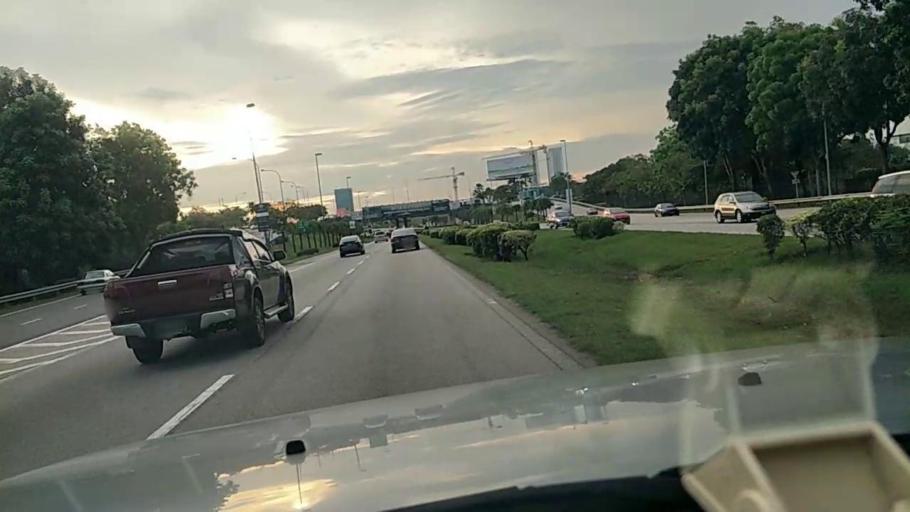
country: MY
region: Selangor
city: Shah Alam
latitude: 3.1033
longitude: 101.4723
